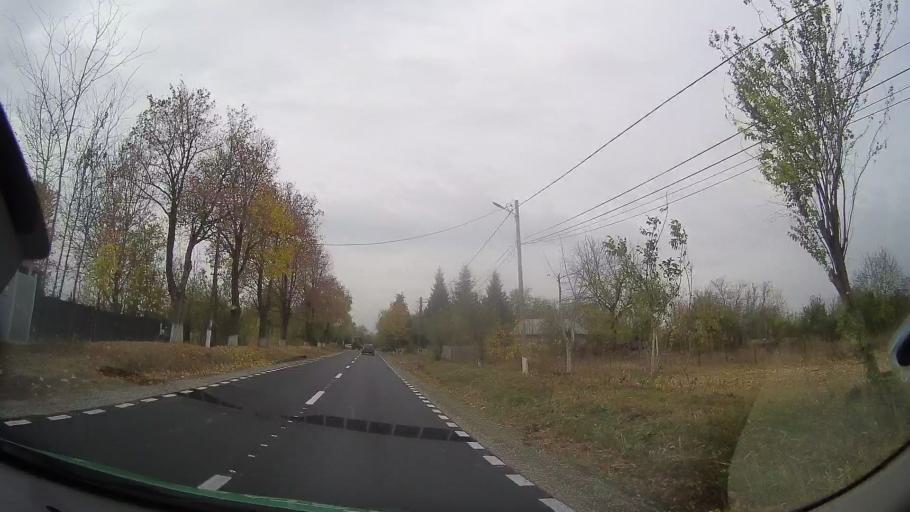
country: RO
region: Ilfov
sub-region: Comuna Nuci
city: Nuci
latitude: 44.7190
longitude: 26.3073
